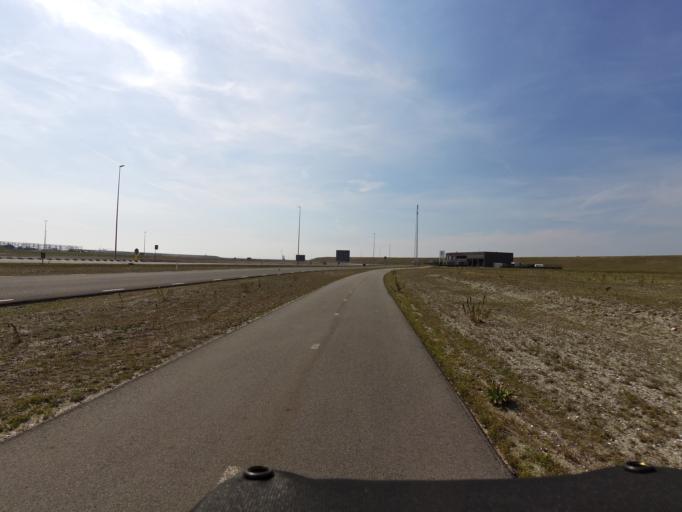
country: NL
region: South Holland
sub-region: Gemeente Rotterdam
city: Hoek van Holland
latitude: 51.9850
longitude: 4.0323
